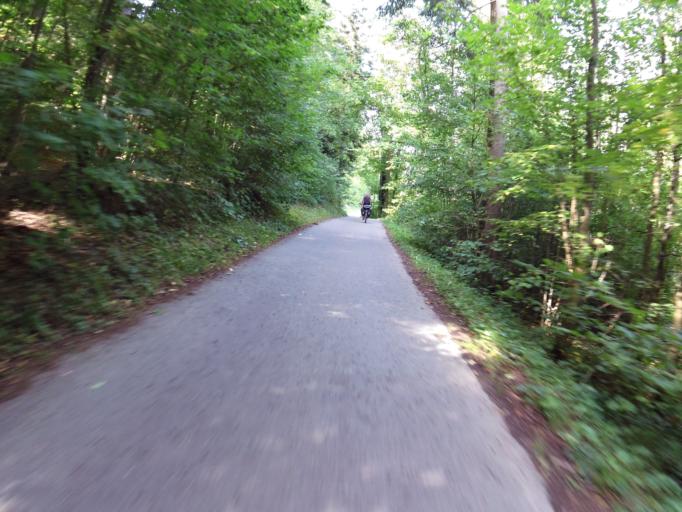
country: DE
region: Baden-Wuerttemberg
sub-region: Karlsruhe Region
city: Horb am Neckar
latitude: 48.4480
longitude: 8.7348
